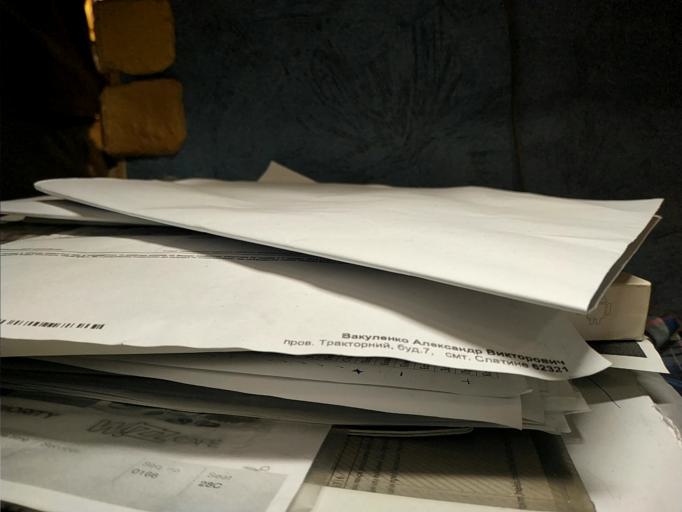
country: RU
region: Tverskaya
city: Zubtsov
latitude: 56.0995
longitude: 34.6918
